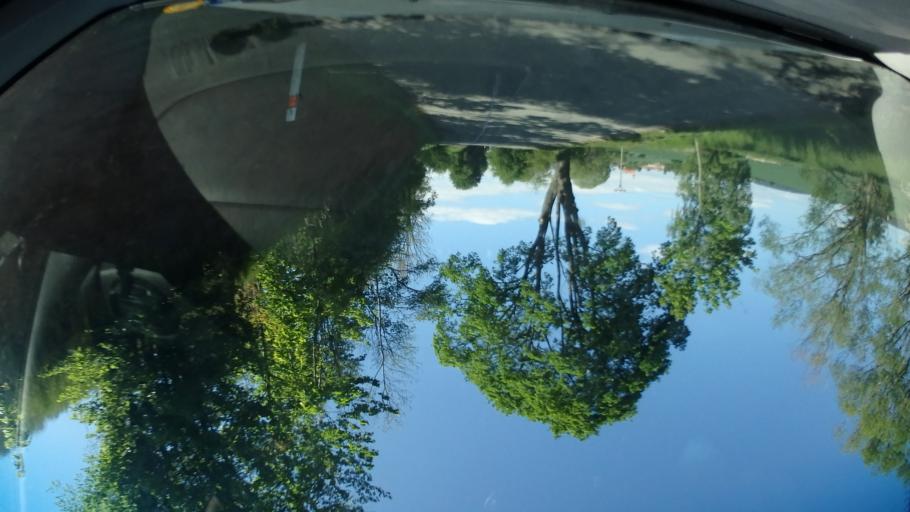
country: CZ
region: South Moravian
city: Velke Opatovice
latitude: 49.6696
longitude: 16.6323
